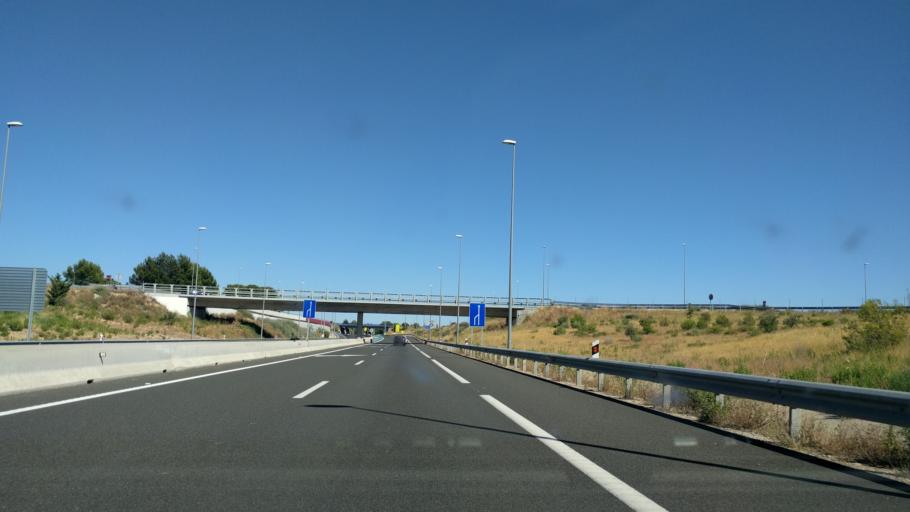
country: ES
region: Catalonia
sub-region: Provincia de Lleida
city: Alpicat
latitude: 41.6485
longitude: 0.5600
